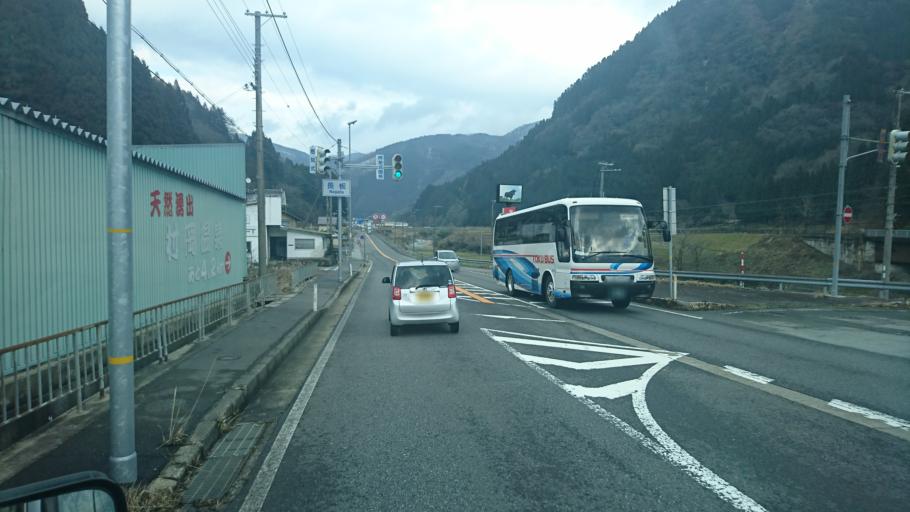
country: JP
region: Hyogo
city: Toyooka
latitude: 35.4896
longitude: 134.5559
